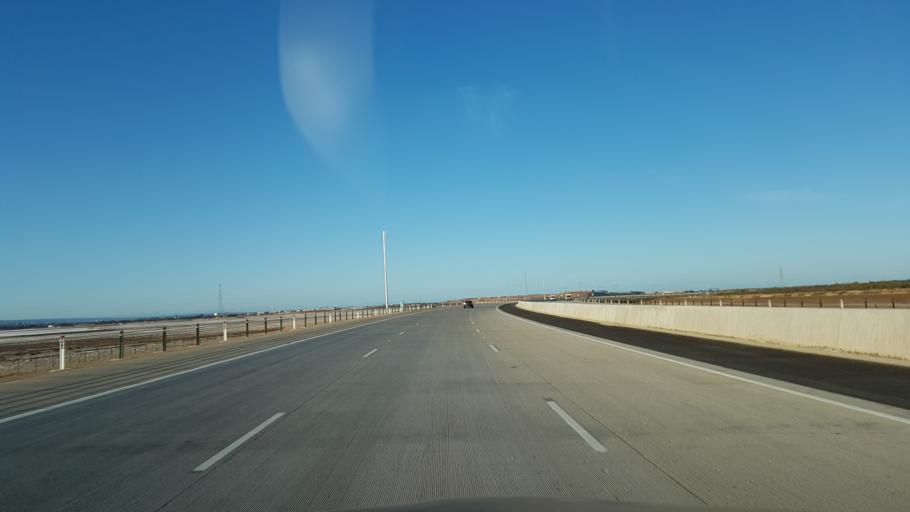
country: AU
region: South Australia
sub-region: Port Adelaide Enfield
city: Enfield
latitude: -34.8022
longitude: 138.5760
